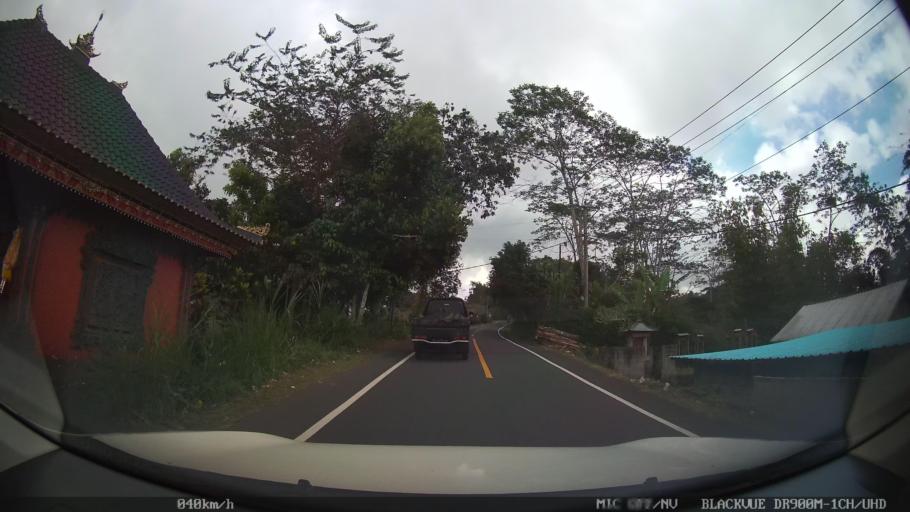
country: ID
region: Bali
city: Banjar Bias
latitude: -8.3291
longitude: 115.4043
